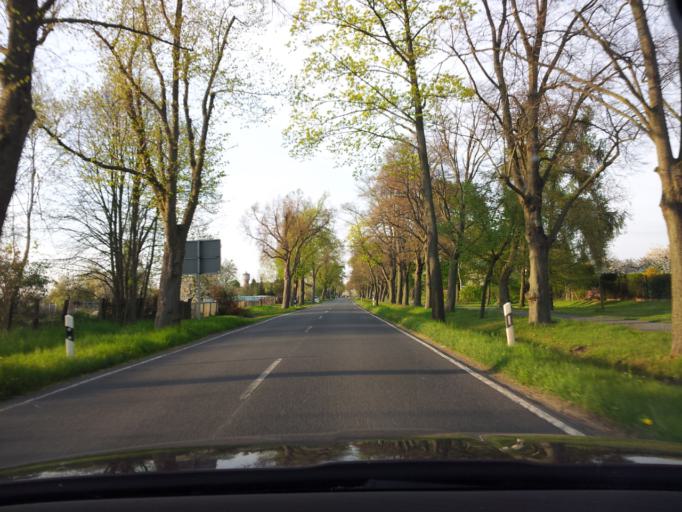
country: DE
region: Brandenburg
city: Dahme
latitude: 51.8603
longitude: 13.4166
